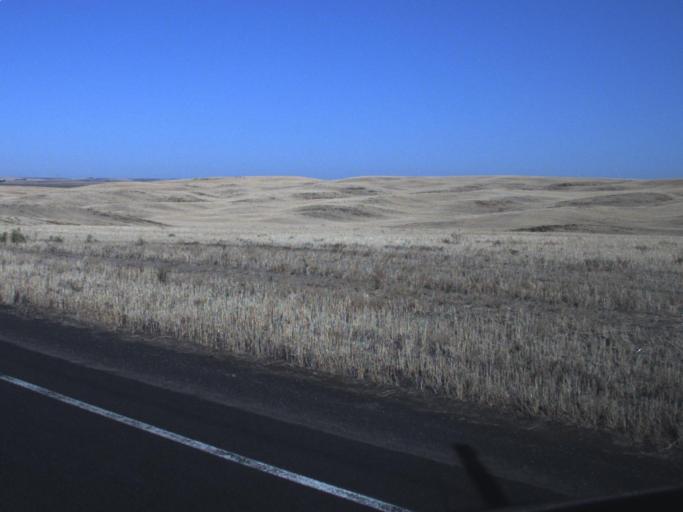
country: US
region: Washington
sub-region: Adams County
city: Ritzville
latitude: 47.0312
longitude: -118.3500
